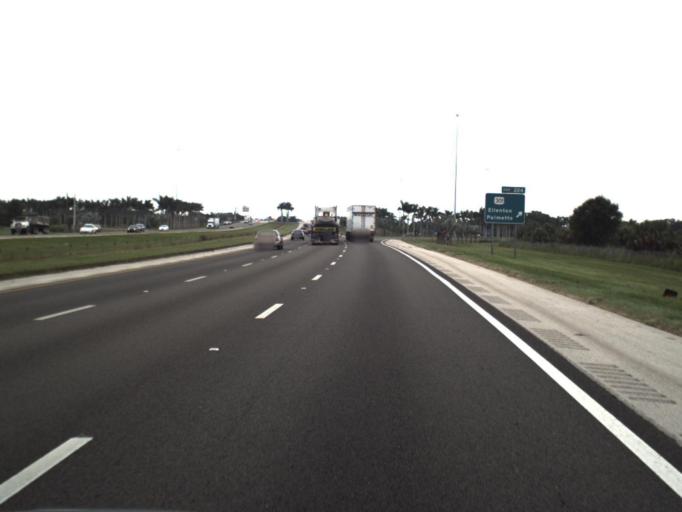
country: US
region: Florida
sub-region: Manatee County
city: Ellenton
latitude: 27.5357
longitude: -82.5106
